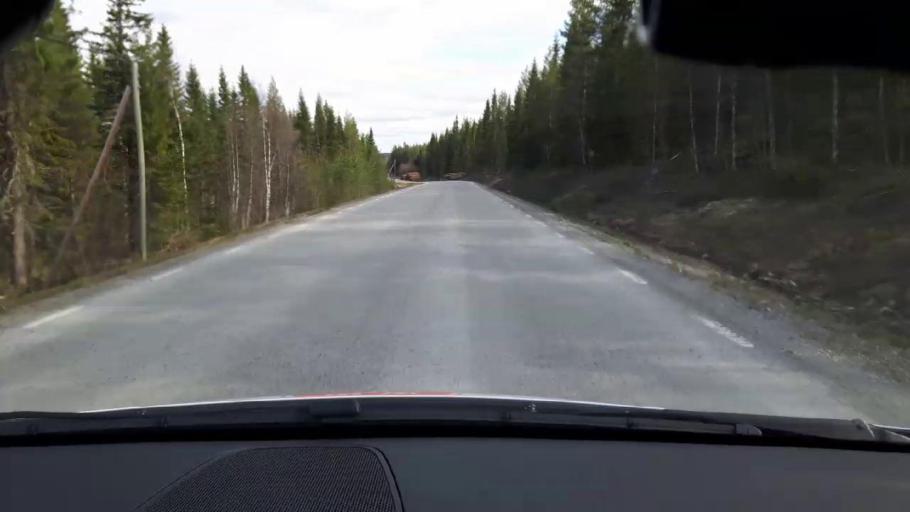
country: SE
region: Jaemtland
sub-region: Bergs Kommun
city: Hoverberg
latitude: 62.7389
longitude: 14.5875
